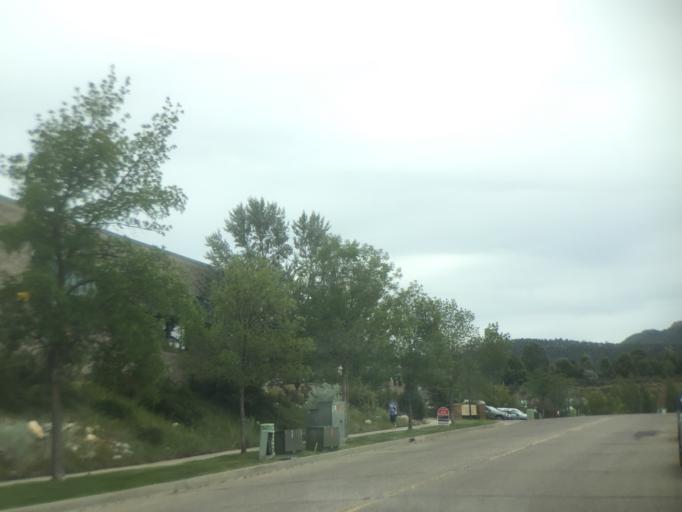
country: US
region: Colorado
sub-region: La Plata County
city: Durango
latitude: 37.2726
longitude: -107.8930
